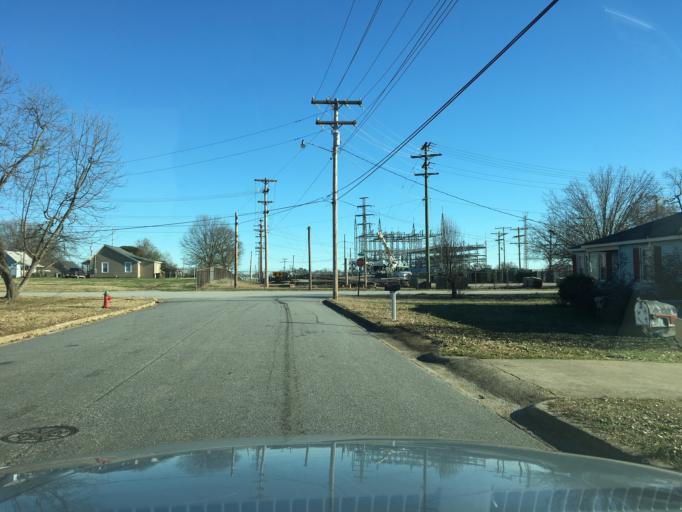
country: US
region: South Carolina
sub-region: Greenville County
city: Greer
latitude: 34.9385
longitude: -82.2357
